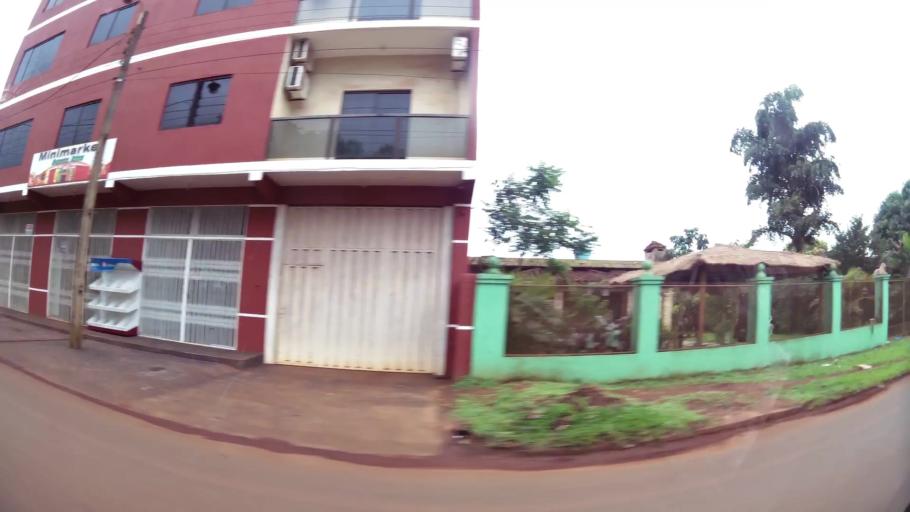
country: PY
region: Alto Parana
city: Presidente Franco
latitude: -25.5151
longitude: -54.6772
